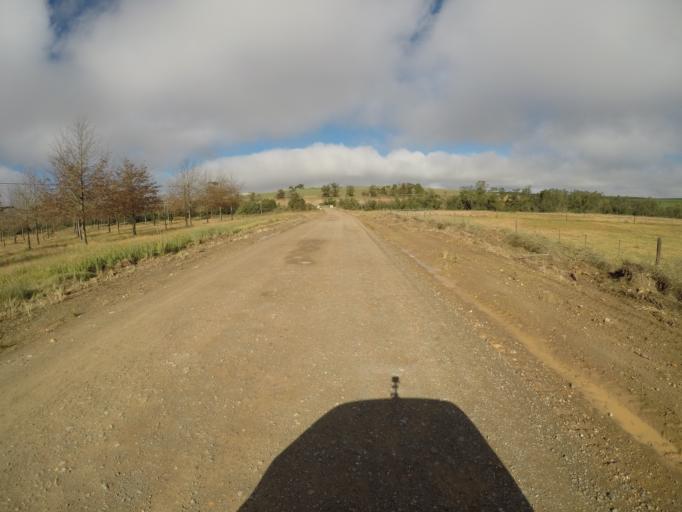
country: ZA
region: Western Cape
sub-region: Cape Winelands District Municipality
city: Ashton
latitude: -34.1270
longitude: 19.8399
